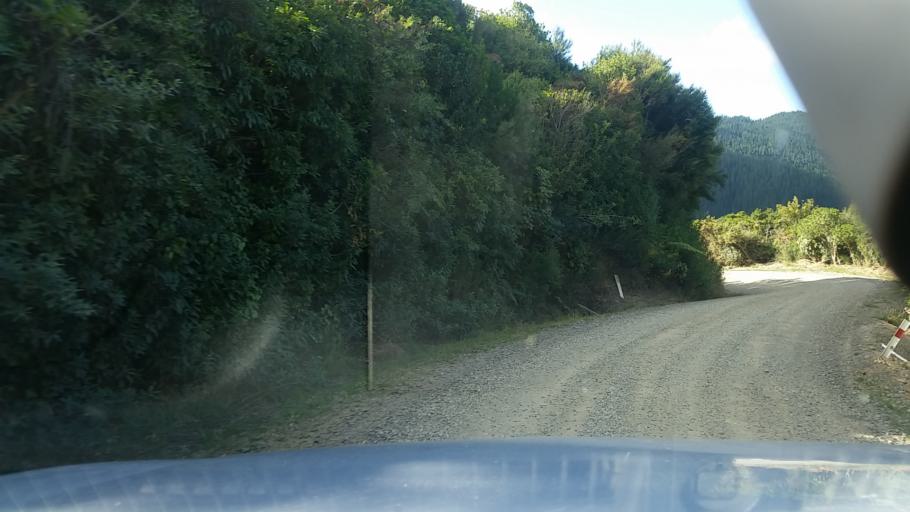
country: NZ
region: Marlborough
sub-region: Marlborough District
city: Picton
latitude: -41.2829
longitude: 174.1439
